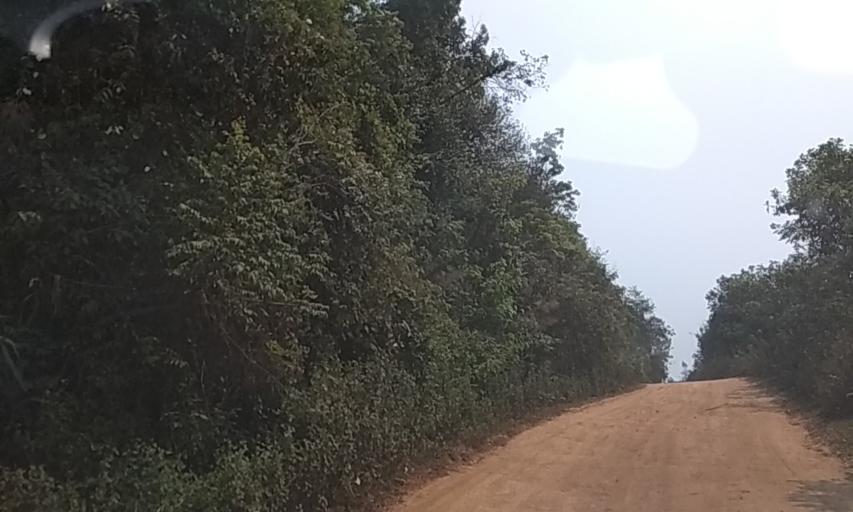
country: TH
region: Nan
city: Chaloem Phra Kiat
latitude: 20.0086
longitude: 101.1257
